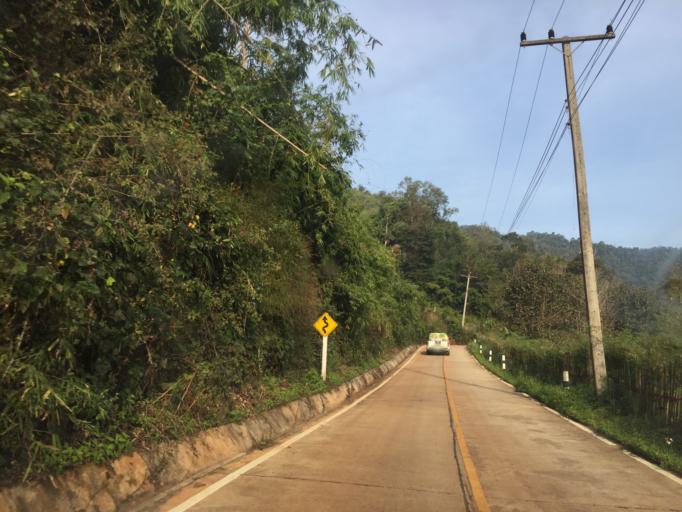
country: TH
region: Chiang Mai
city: Samoeng
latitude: 18.9838
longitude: 98.7067
